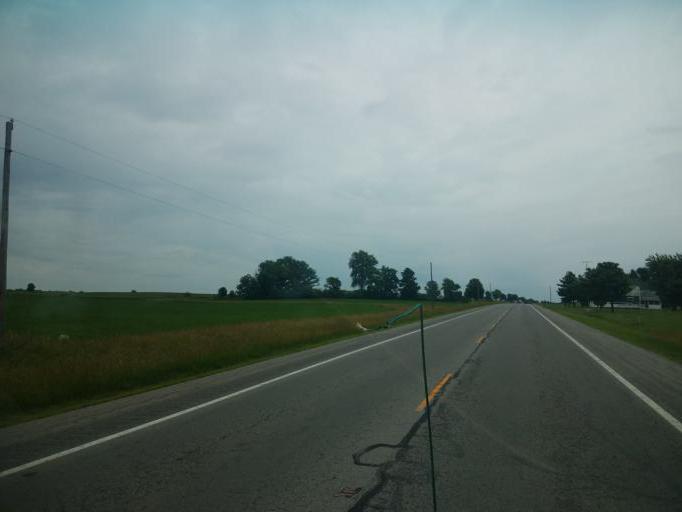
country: US
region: Ohio
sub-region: Hardin County
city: Kenton
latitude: 40.6945
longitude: -83.7047
